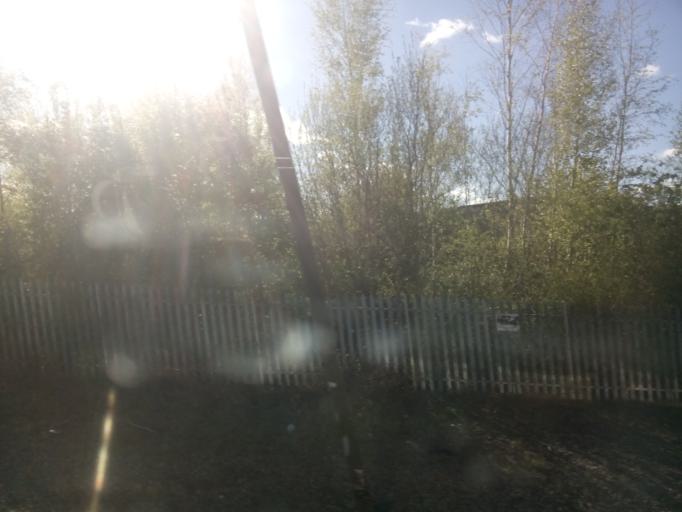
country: GB
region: England
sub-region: Darlington
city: Darlington
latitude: 54.5341
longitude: -1.5430
